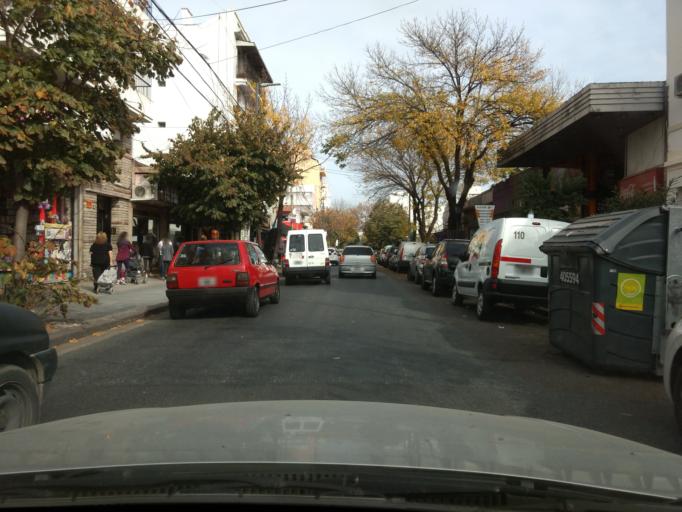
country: AR
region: Buenos Aires F.D.
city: Villa Santa Rita
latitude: -34.6195
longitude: -58.5053
